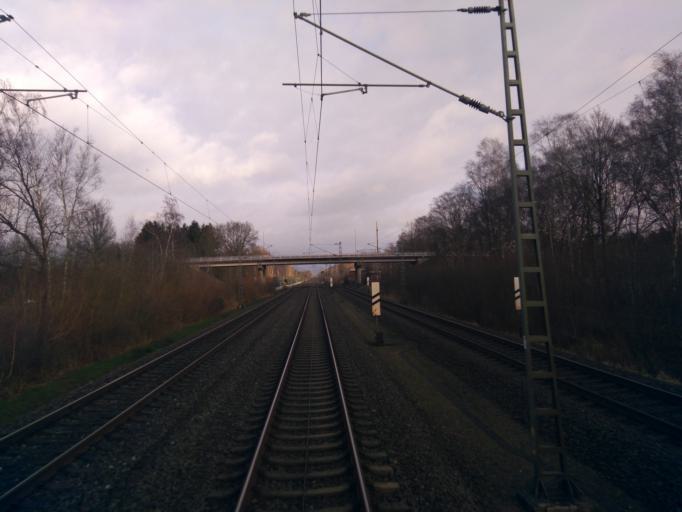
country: DE
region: Lower Saxony
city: Konigsmoor
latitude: 53.2301
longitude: 9.6414
